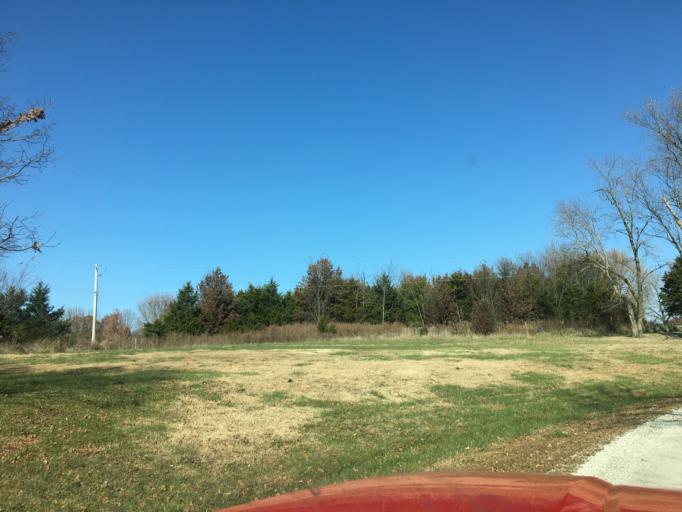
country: US
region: Missouri
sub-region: Cole County
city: Wardsville
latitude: 38.4823
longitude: -92.1783
